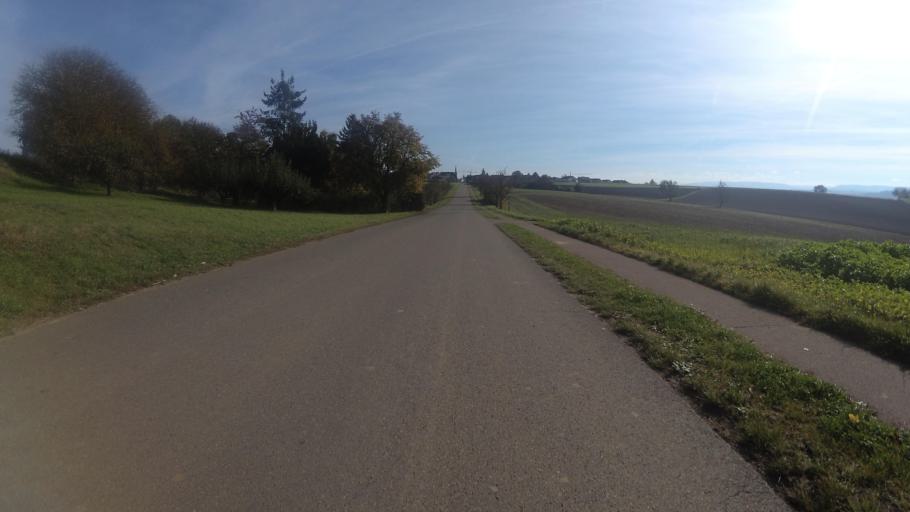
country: DE
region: Baden-Wuerttemberg
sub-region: Regierungsbezirk Stuttgart
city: Neudenau
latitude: 49.2642
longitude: 9.2877
